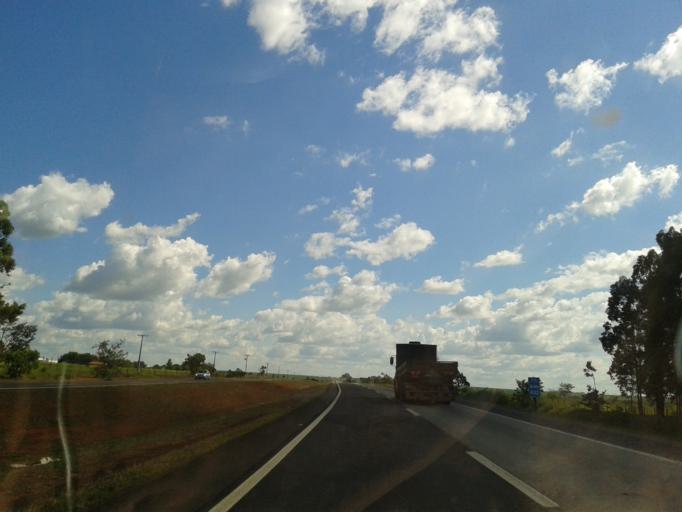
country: BR
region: Goias
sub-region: Morrinhos
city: Morrinhos
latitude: -17.8018
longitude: -49.2067
